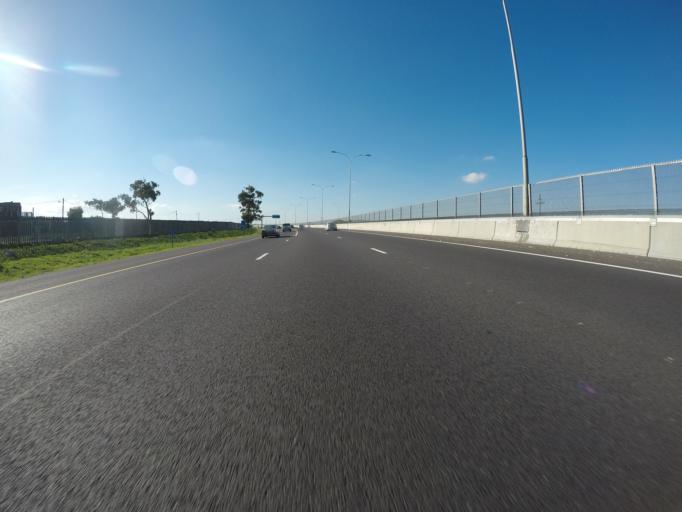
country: ZA
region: Western Cape
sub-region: City of Cape Town
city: Lansdowne
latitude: -33.9849
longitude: 18.6497
